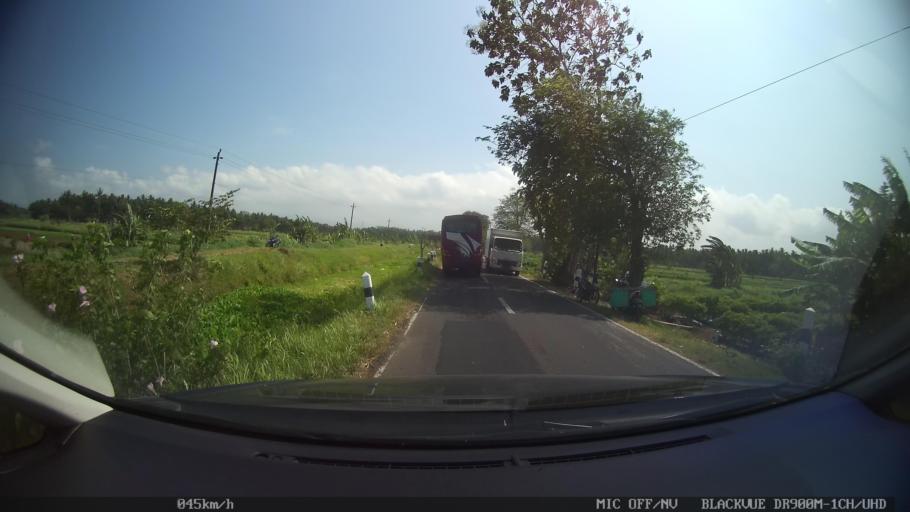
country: ID
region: Daerah Istimewa Yogyakarta
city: Srandakan
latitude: -7.9327
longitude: 110.1556
